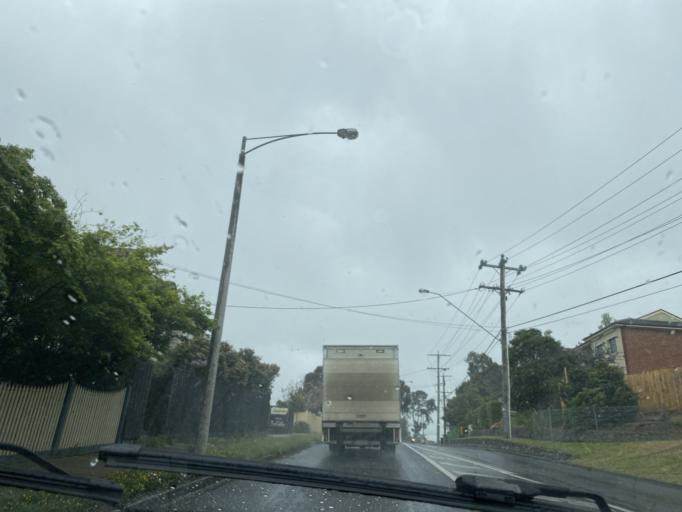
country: AU
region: Victoria
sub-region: Banyule
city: Lower Plenty
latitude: -37.7251
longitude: 145.1121
